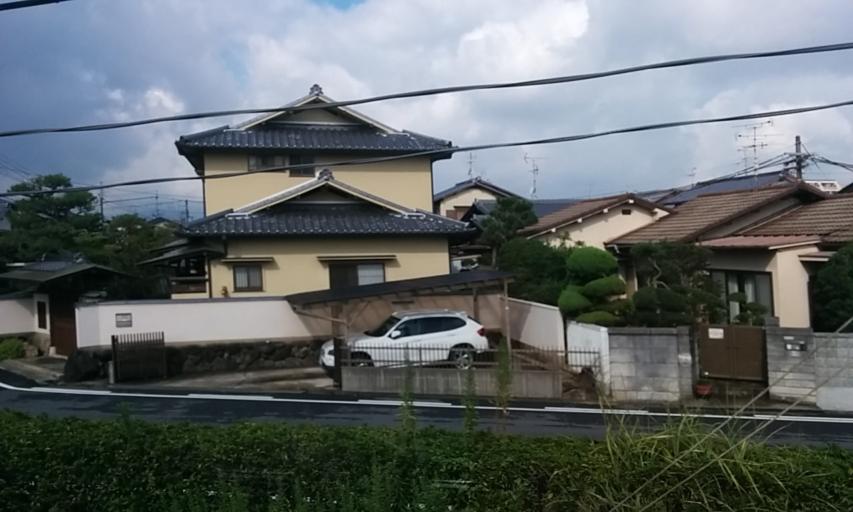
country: JP
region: Nara
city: Nara-shi
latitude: 34.6877
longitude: 135.7853
